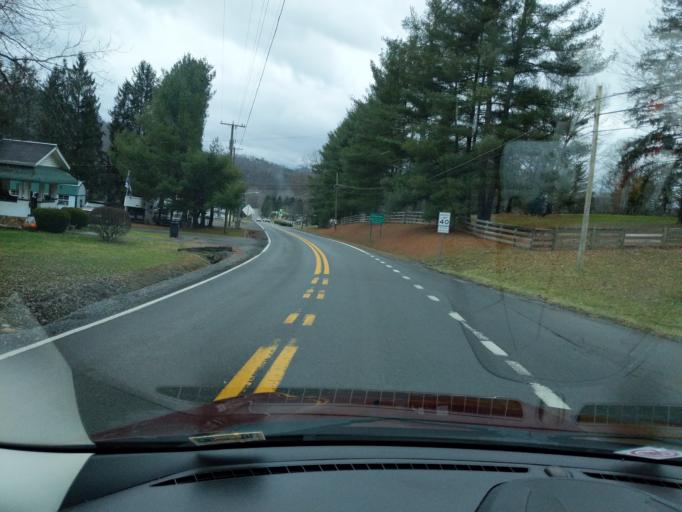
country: US
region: West Virginia
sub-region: Greenbrier County
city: Alderson
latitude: 37.7316
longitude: -80.6306
